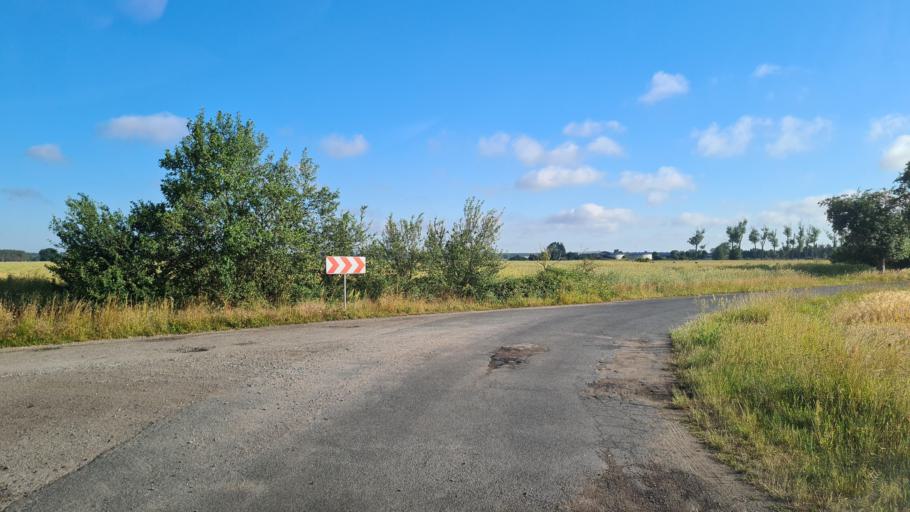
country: DE
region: Saxony
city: Beilrode
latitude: 51.6294
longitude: 13.1153
